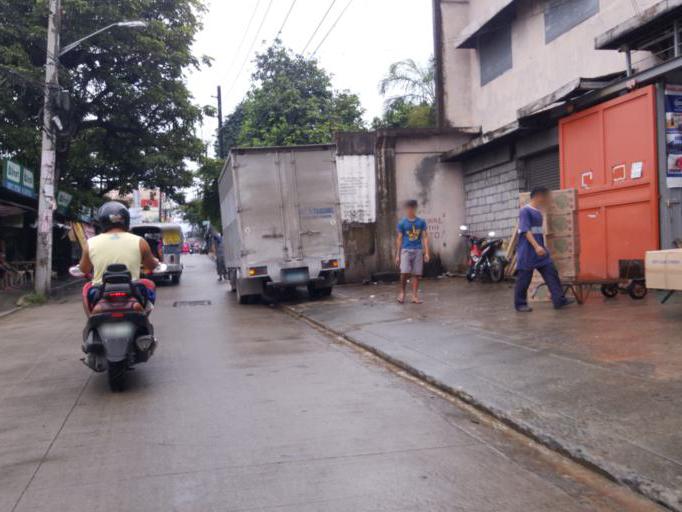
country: PH
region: Calabarzon
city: Bagong Pagasa
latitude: 14.7205
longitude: 121.0414
